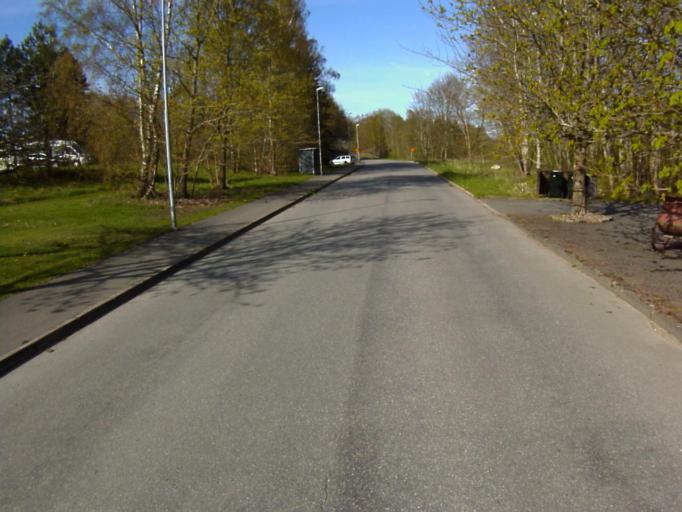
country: SE
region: Skane
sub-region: Kristianstads Kommun
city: Onnestad
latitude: 55.9943
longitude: 14.0367
